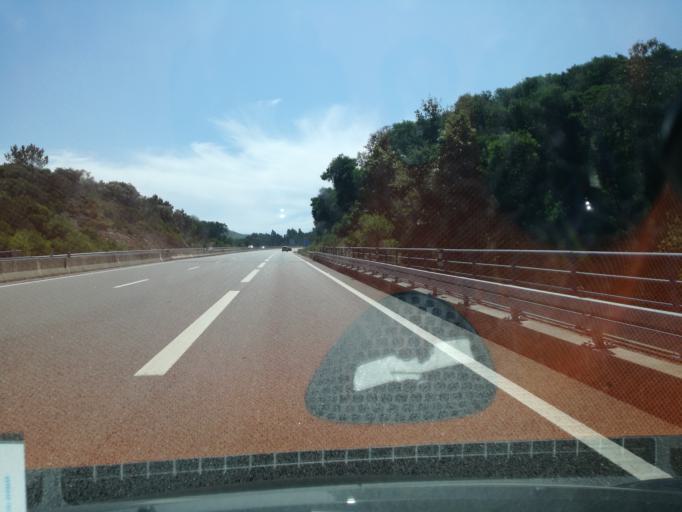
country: PT
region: Viana do Castelo
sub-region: Caminha
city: Vila Praia de Ancora
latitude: 41.7978
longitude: -8.7961
